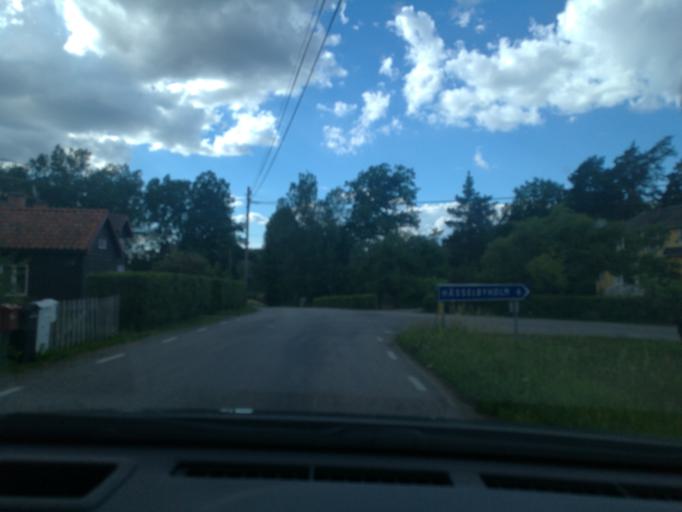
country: SE
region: Soedermanland
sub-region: Eskilstuna Kommun
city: Arla
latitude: 59.4465
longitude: 16.7790
